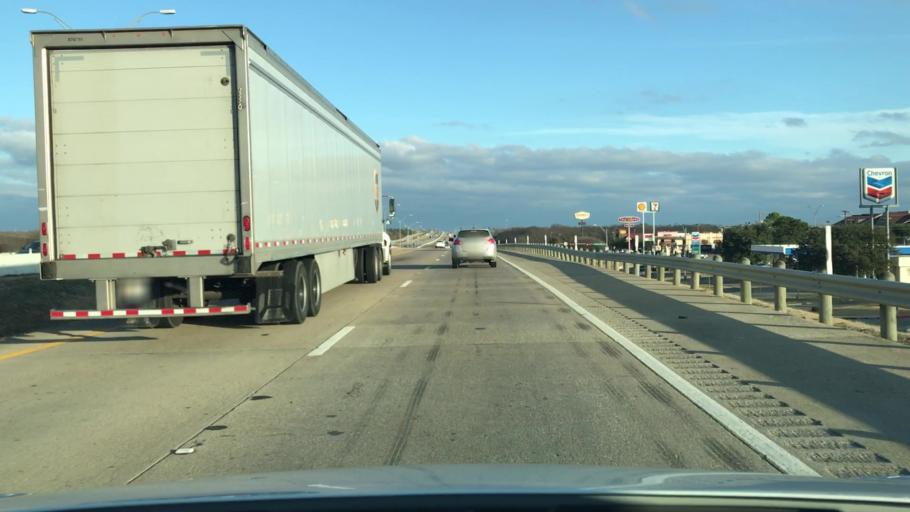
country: US
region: Texas
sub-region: Dallas County
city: Mesquite
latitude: 32.7907
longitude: -96.5976
